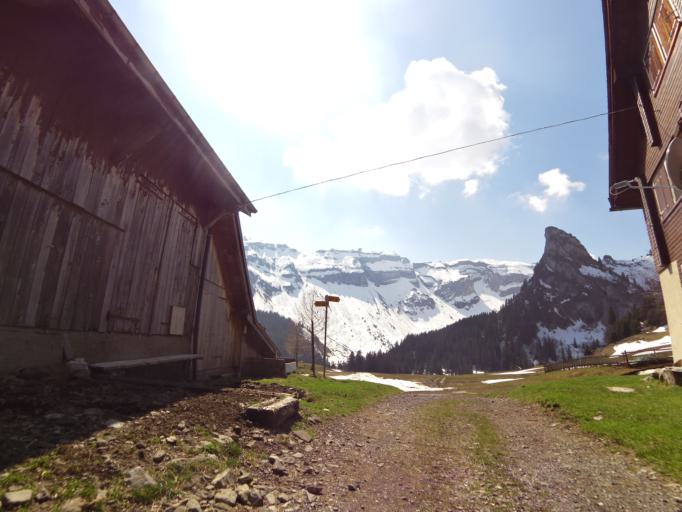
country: CH
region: Nidwalden
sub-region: Nidwalden
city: Emmetten
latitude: 46.9026
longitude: 8.4973
